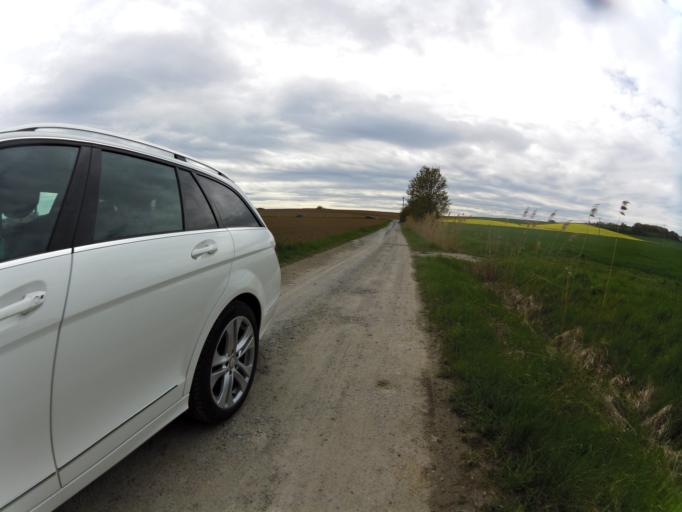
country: DE
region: Bavaria
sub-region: Regierungsbezirk Unterfranken
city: Prosselsheim
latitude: 49.8491
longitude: 10.1473
